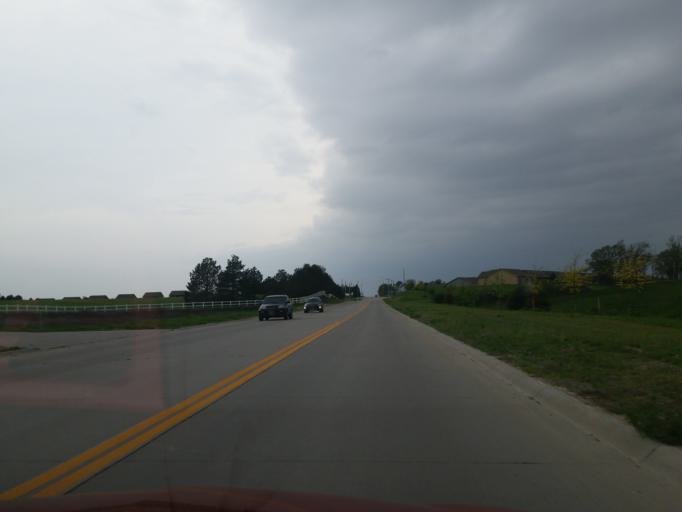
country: US
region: Nebraska
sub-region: Douglas County
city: Bennington
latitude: 41.3212
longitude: -96.1300
